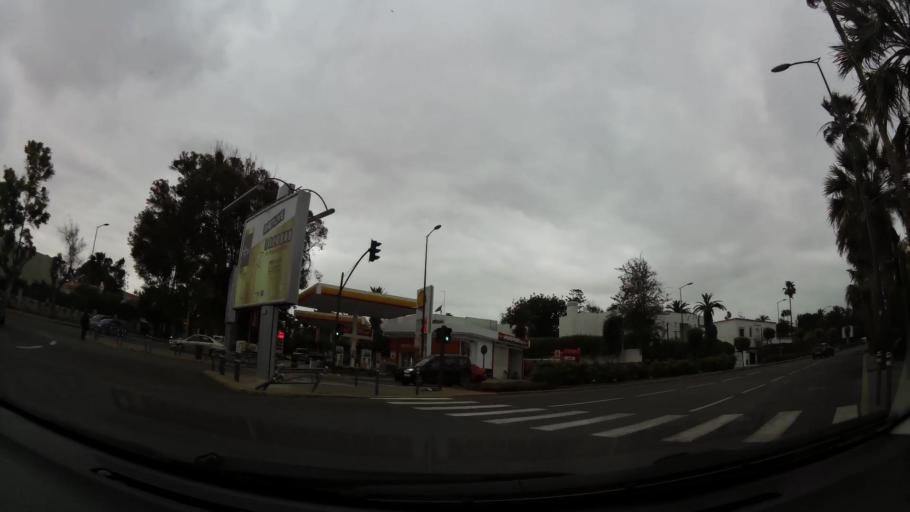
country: MA
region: Grand Casablanca
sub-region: Casablanca
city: Casablanca
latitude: 33.5914
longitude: -7.6571
